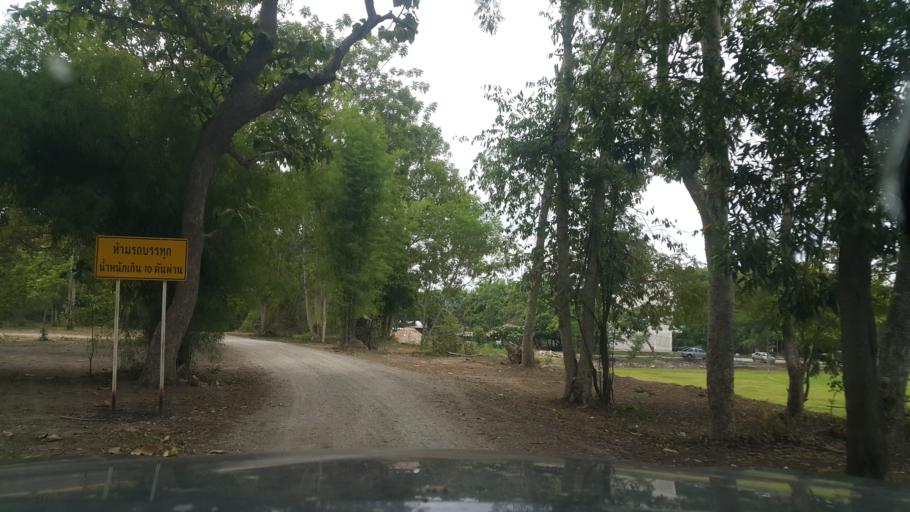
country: TH
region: Chiang Mai
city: San Pa Tong
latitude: 18.6489
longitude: 98.8482
